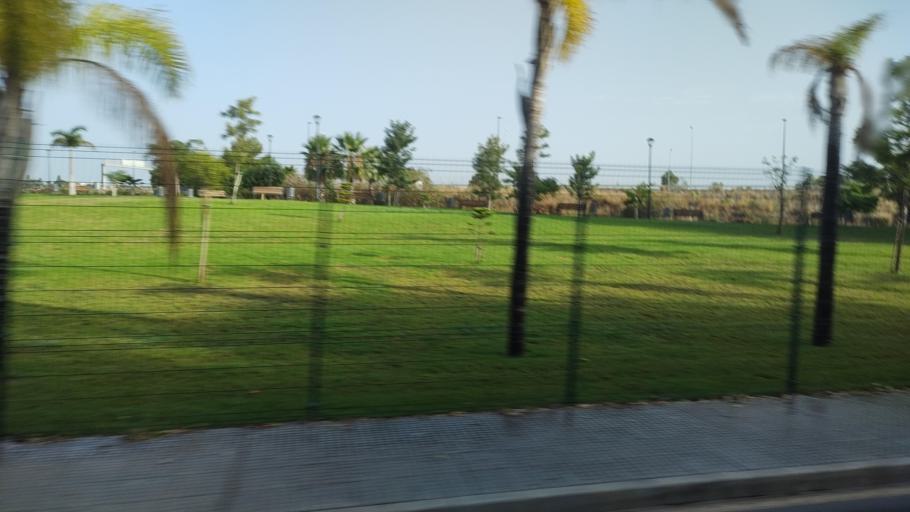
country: ES
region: Andalusia
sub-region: Provincia de Malaga
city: Torremolinos
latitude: 36.6479
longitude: -4.4830
